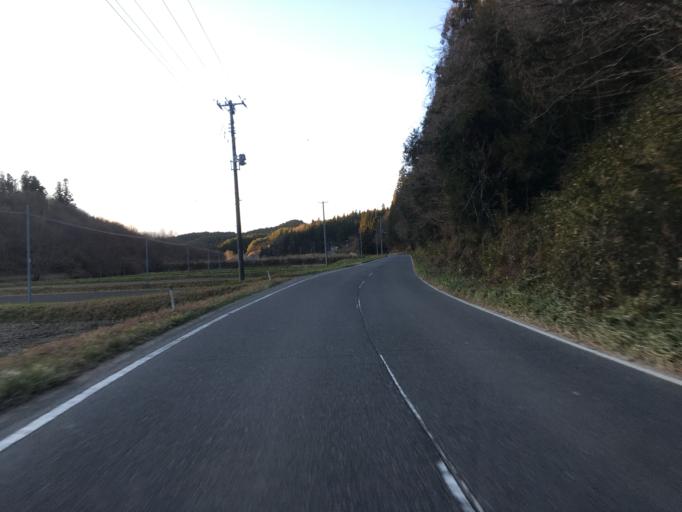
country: JP
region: Fukushima
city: Ishikawa
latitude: 37.2707
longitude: 140.5785
